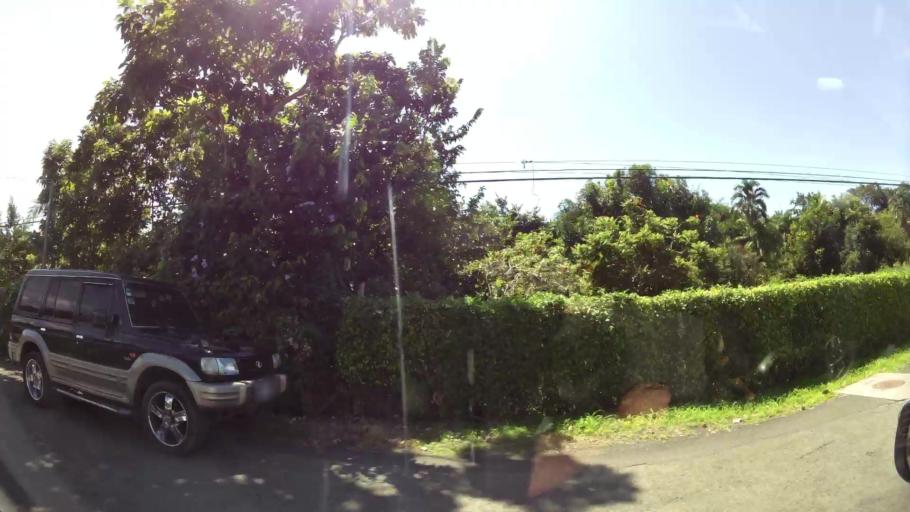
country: CR
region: Puntarenas
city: Quepos
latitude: 9.3302
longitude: -83.9559
